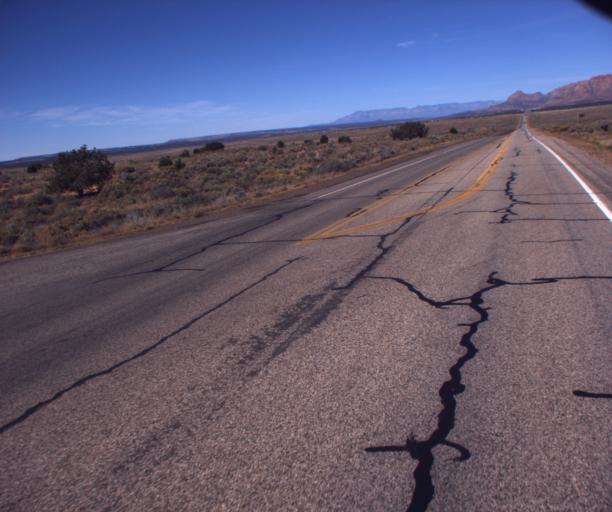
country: US
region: Arizona
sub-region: Mohave County
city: Colorado City
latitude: 36.9040
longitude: -112.9221
